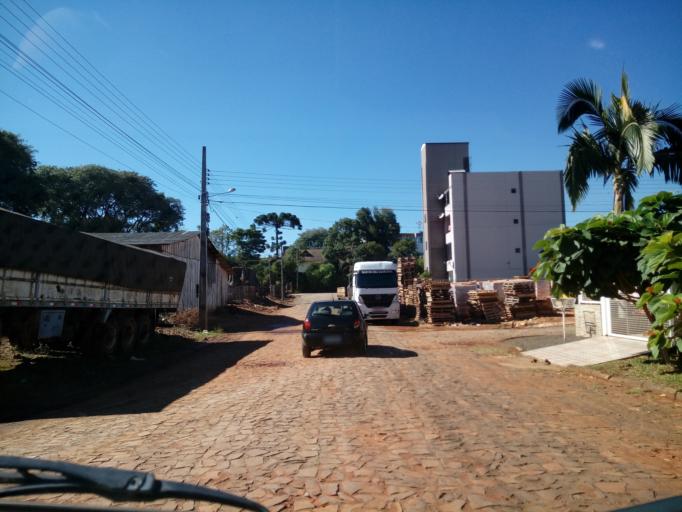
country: BR
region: Santa Catarina
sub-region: Chapeco
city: Chapeco
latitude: -27.0965
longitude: -52.6755
